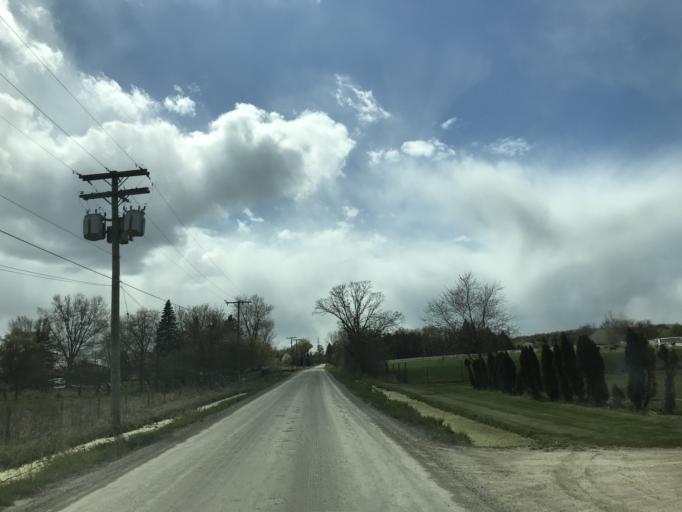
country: US
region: Michigan
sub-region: Oakland County
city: South Lyon
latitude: 42.3764
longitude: -83.6142
